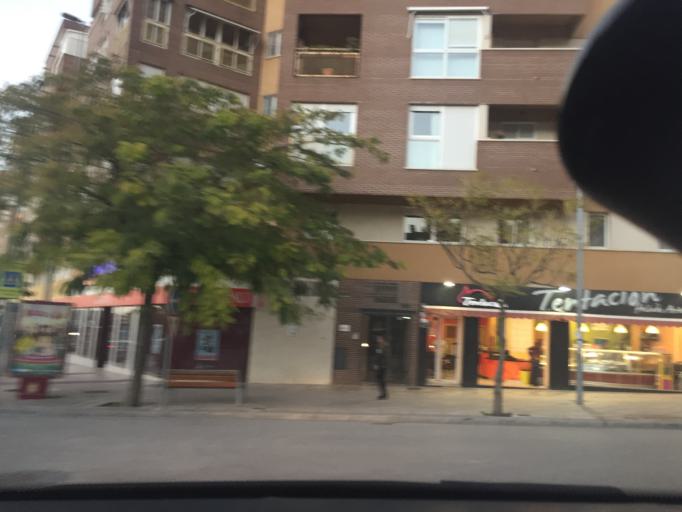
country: ES
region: Andalusia
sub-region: Provincia de Jaen
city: Jaen
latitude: 37.7829
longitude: -3.7895
